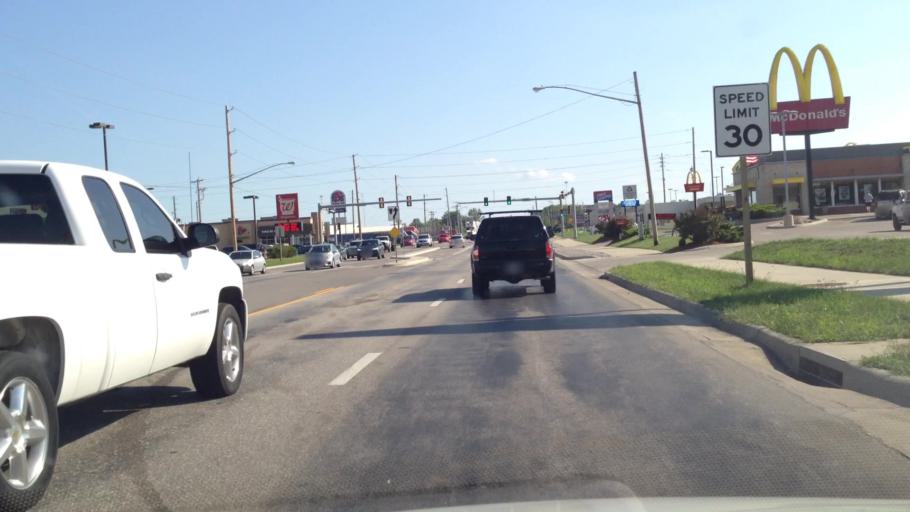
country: US
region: Kansas
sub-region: Bourbon County
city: Fort Scott
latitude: 37.8142
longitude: -94.7055
